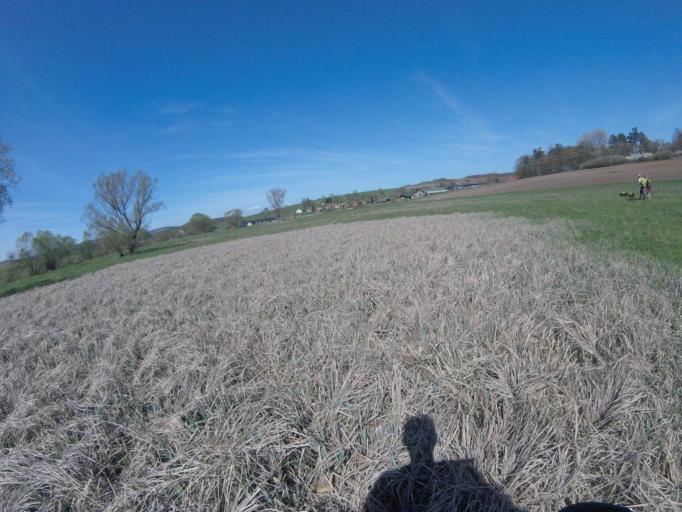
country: HU
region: Borsod-Abauj-Zemplen
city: Szendro
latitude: 48.4139
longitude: 20.7751
